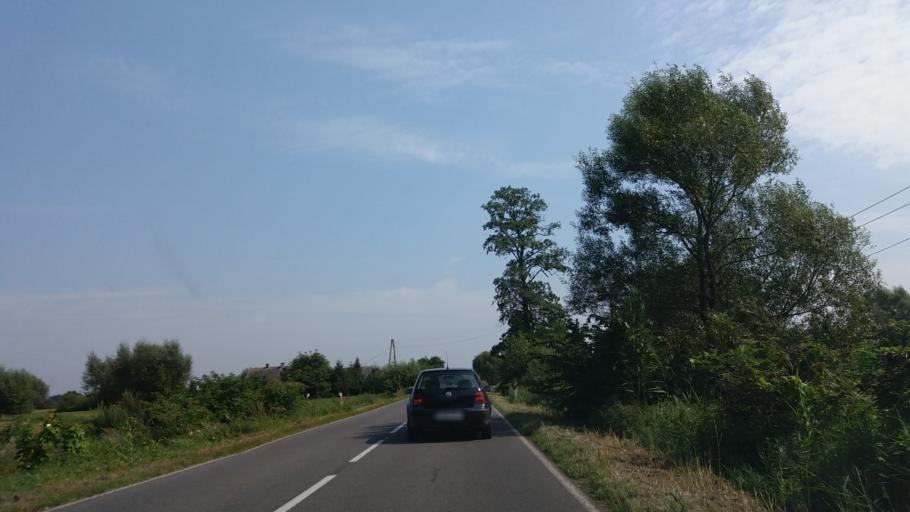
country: PL
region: Lubusz
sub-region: Powiat strzelecko-drezdenecki
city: Zwierzyn
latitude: 52.8215
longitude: 15.6199
